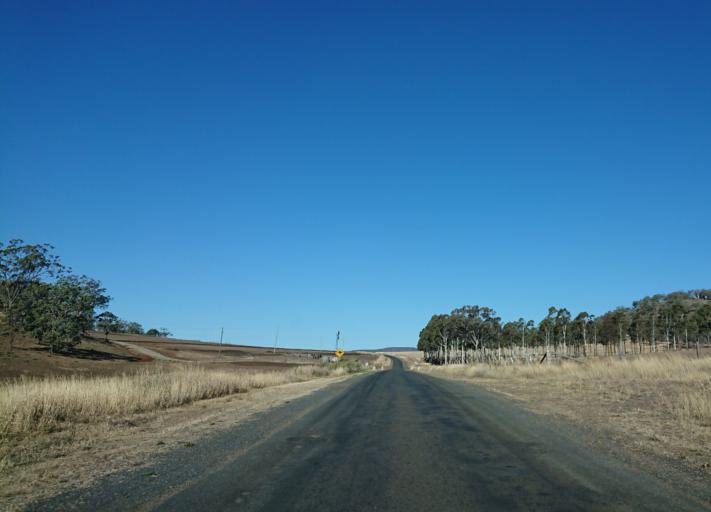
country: AU
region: Queensland
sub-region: Toowoomba
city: Top Camp
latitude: -27.8278
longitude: 152.0348
